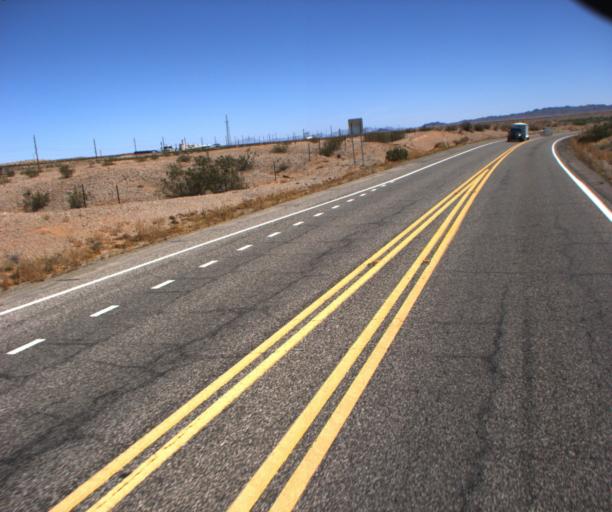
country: US
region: Arizona
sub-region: La Paz County
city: Parker
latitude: 34.0020
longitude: -114.2319
